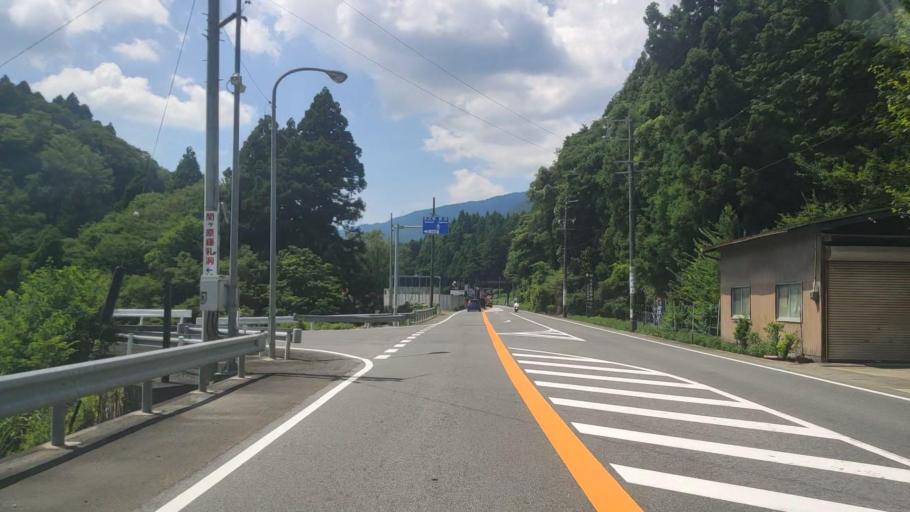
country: JP
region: Gifu
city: Tarui
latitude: 35.3791
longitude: 136.4383
